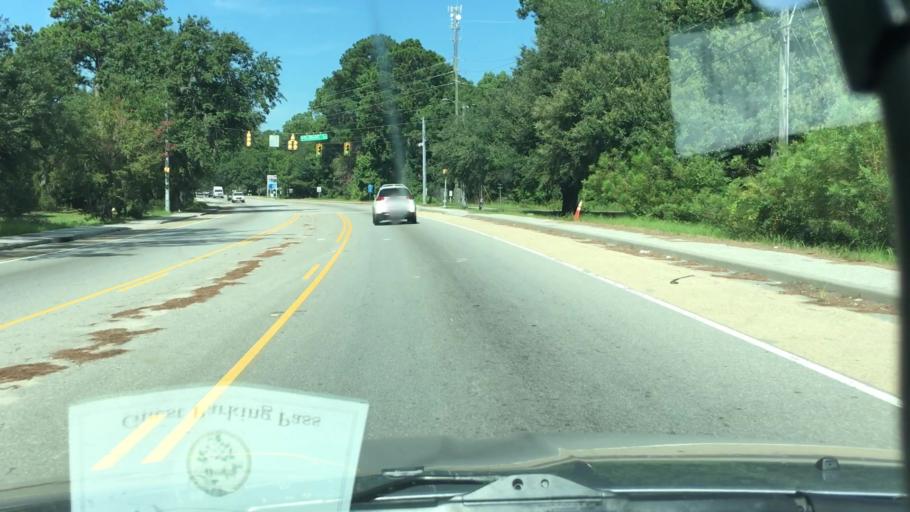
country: US
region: South Carolina
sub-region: Beaufort County
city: Beaufort
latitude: 32.3968
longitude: -80.5798
